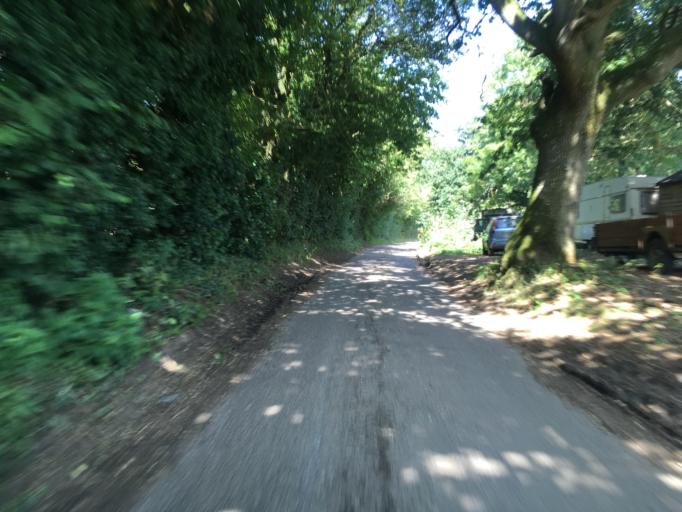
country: GB
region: England
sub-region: Hampshire
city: Highclere
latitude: 51.3019
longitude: -1.3820
